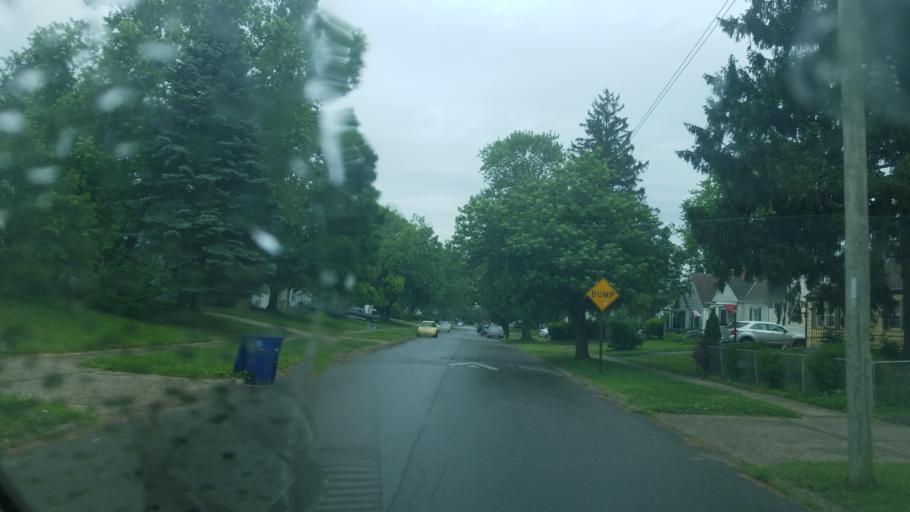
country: US
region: Ohio
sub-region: Franklin County
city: Worthington
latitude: 40.0366
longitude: -82.9945
